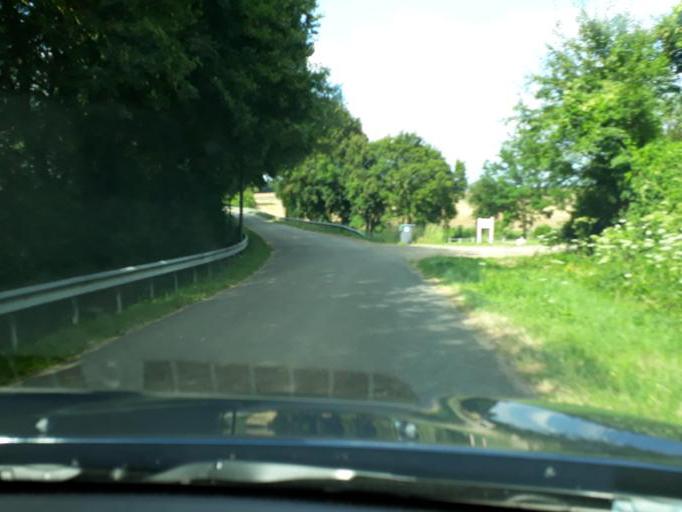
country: FR
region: Centre
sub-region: Departement du Cher
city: Jouet-sur-l'Aubois
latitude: 47.0025
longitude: 2.9129
